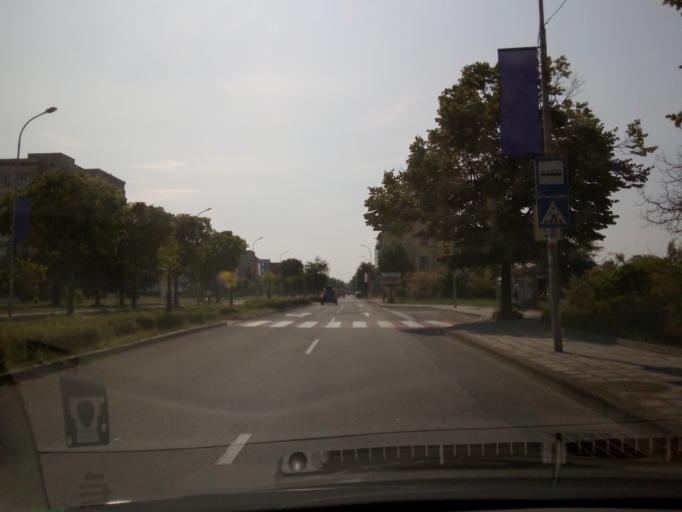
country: BG
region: Burgas
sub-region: Obshtina Pomorie
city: Pomorie
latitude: 42.5625
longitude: 27.6304
